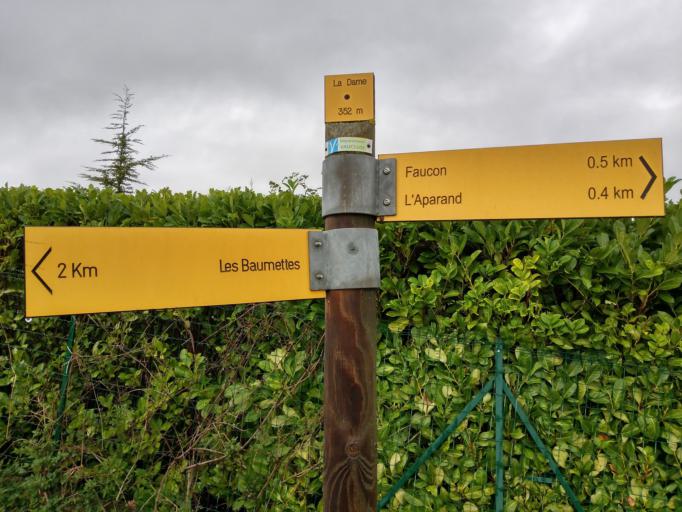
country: FR
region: Rhone-Alpes
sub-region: Departement de la Drome
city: Mirabel-aux-Baronnies
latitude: 44.2558
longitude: 5.1451
